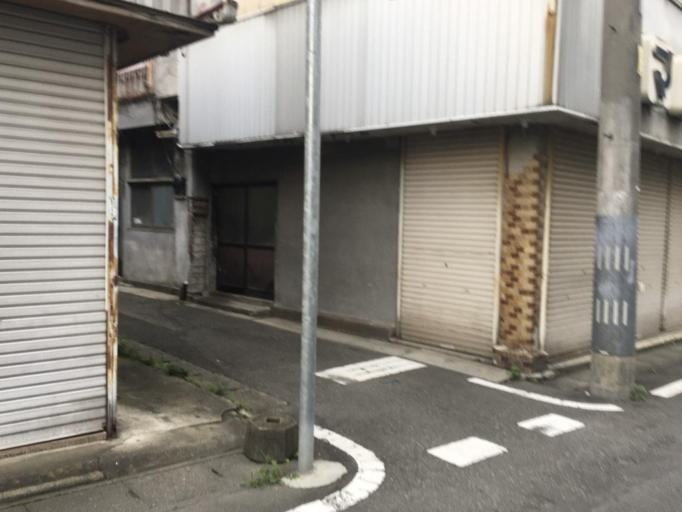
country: JP
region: Gunma
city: Isesaki
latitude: 36.3195
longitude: 139.1947
